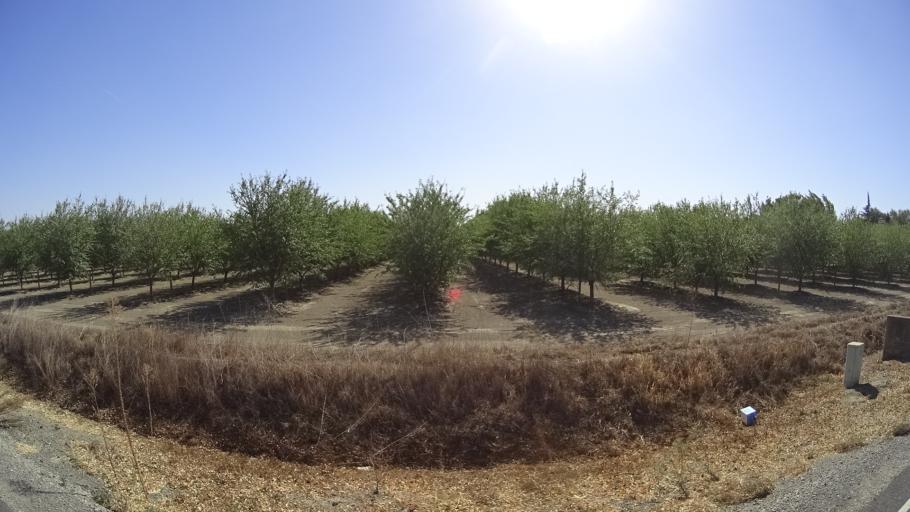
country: US
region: California
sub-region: Yolo County
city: Davis
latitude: 38.5906
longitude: -121.8326
